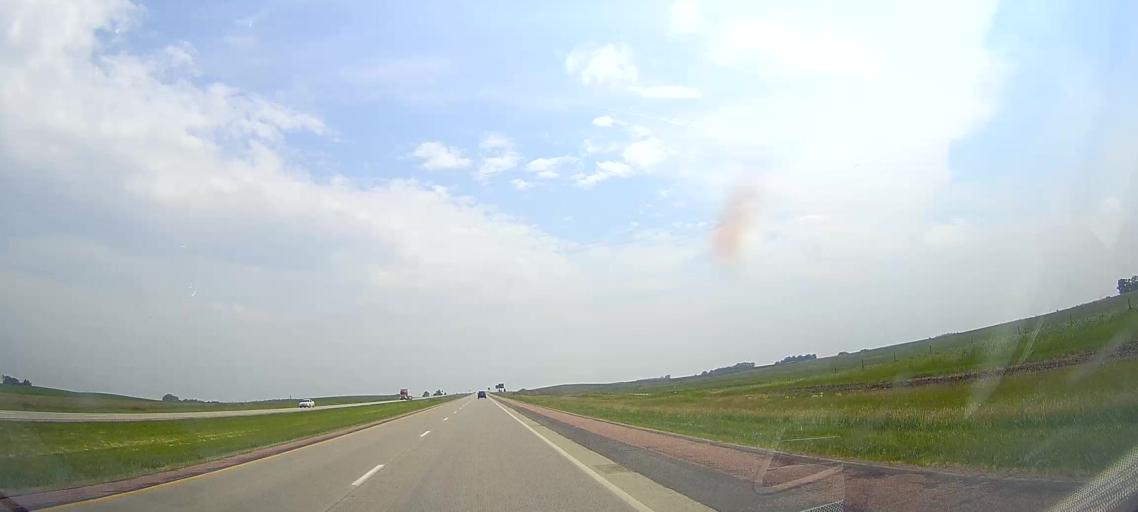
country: US
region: South Dakota
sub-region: Union County
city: Beresford
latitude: 43.0188
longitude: -96.7959
